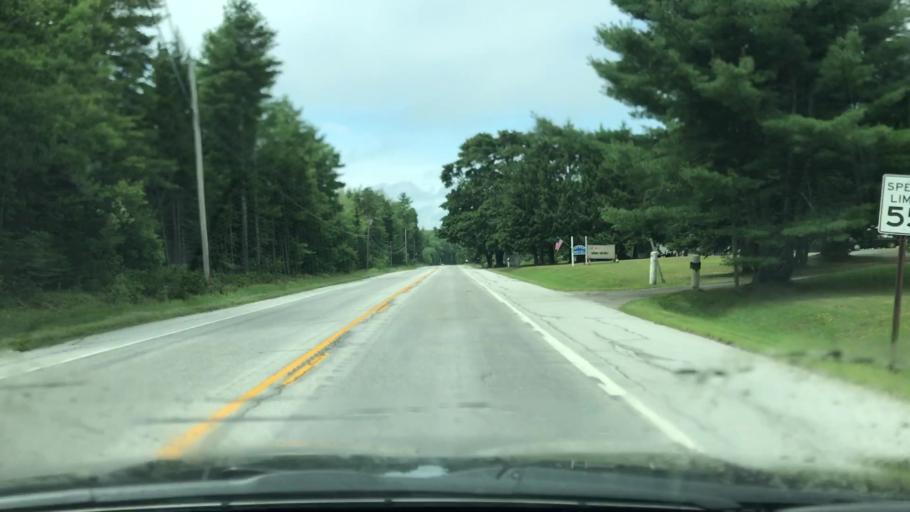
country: US
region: Maine
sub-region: Waldo County
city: Northport
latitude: 44.3386
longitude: -68.9630
